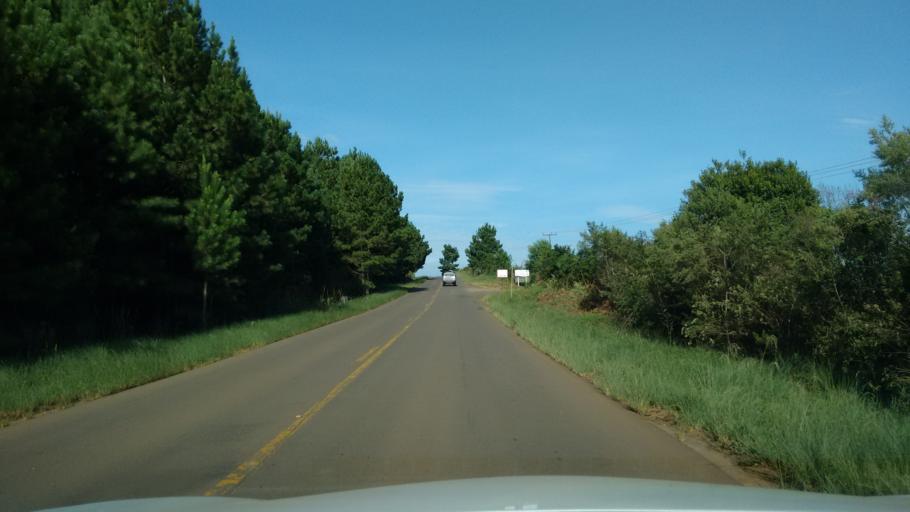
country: BR
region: Santa Catarina
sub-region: Videira
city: Videira
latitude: -27.0869
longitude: -50.9052
